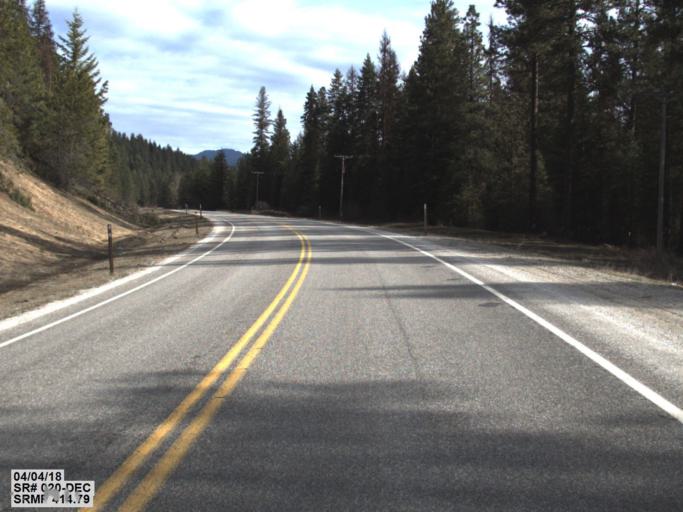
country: US
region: Washington
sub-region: Pend Oreille County
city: Newport
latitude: 48.3974
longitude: -117.3134
